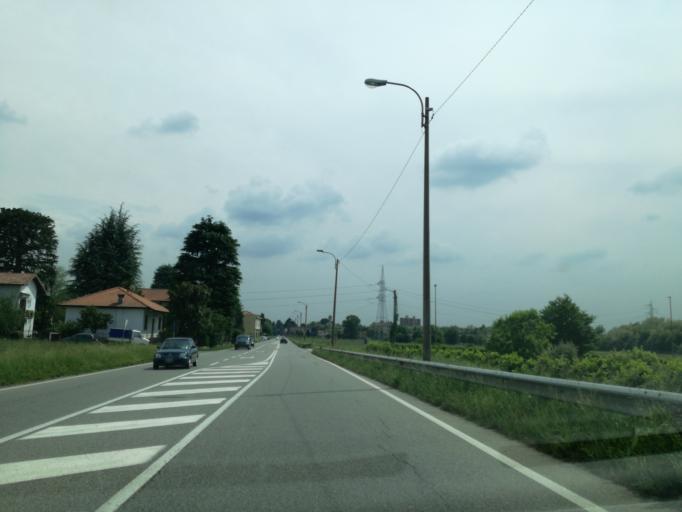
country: IT
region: Lombardy
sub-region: Provincia di Monza e Brianza
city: Carate Brianza
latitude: 45.6675
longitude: 9.2455
